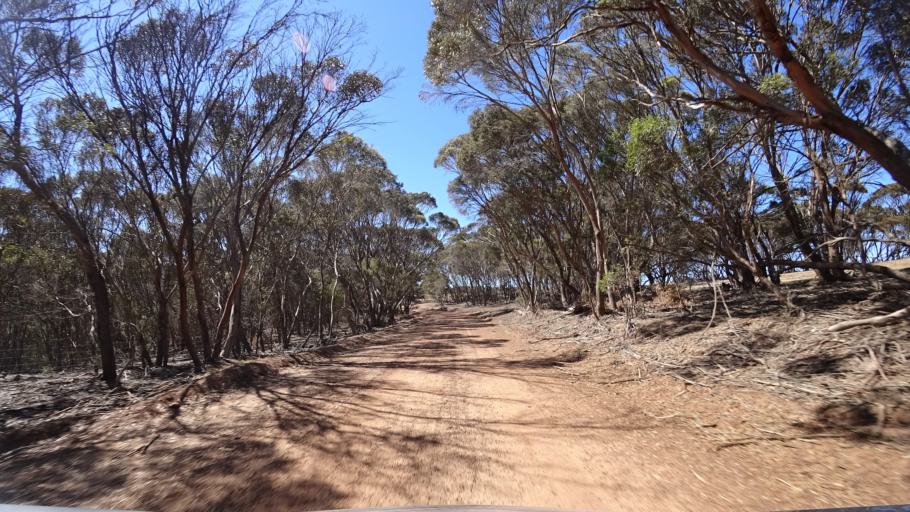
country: AU
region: South Australia
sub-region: Kangaroo Island
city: Kingscote
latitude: -35.7488
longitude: 137.7270
